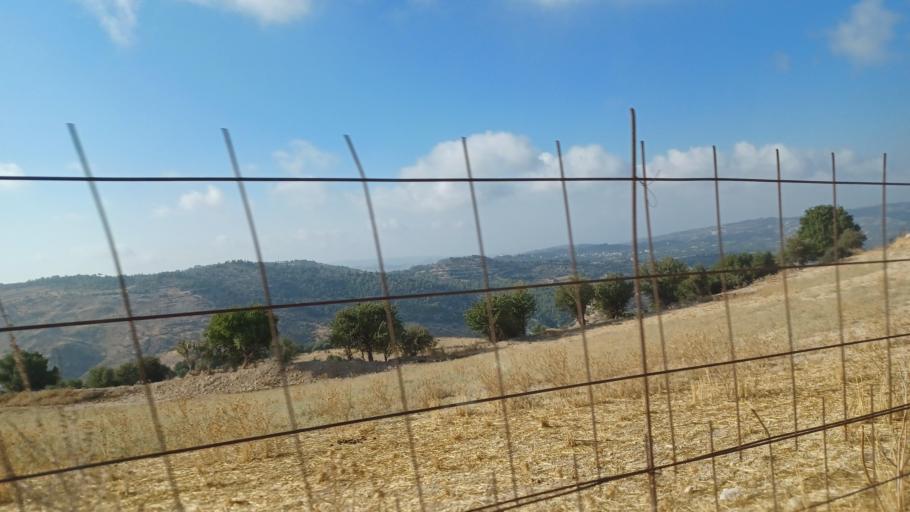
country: CY
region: Pafos
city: Mesogi
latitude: 34.8568
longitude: 32.5868
